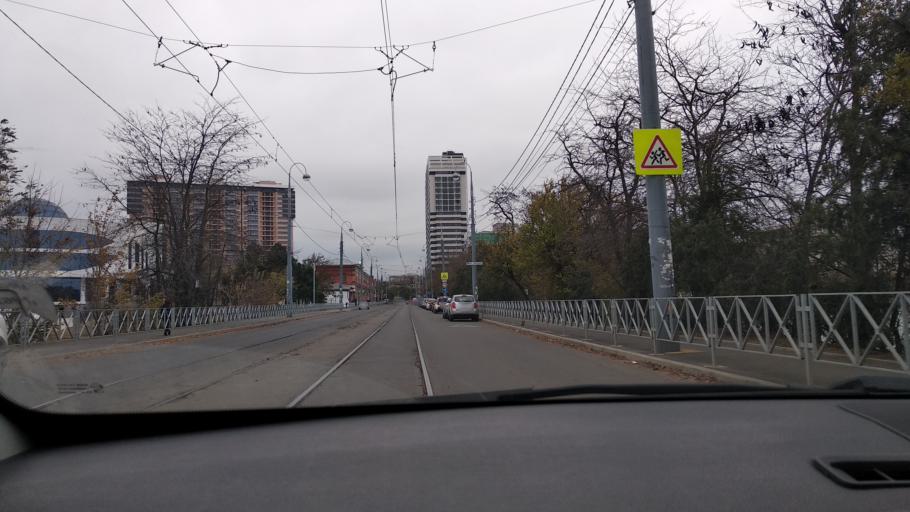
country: RU
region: Krasnodarskiy
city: Krasnodar
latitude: 45.0270
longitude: 38.9905
